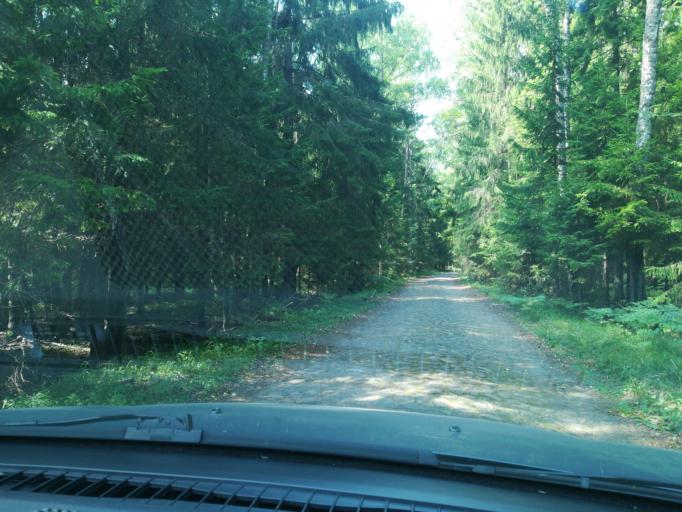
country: RU
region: Leningrad
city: Ust'-Luga
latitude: 59.7683
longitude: 28.1708
